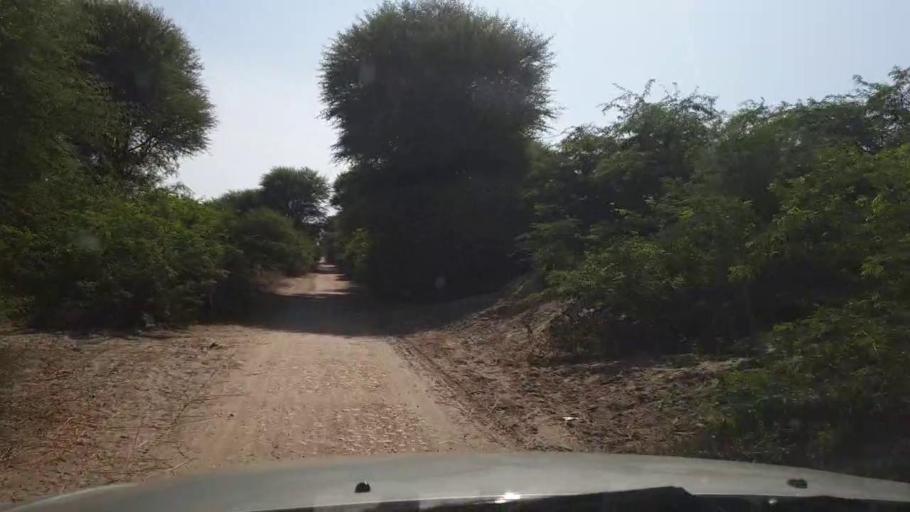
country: PK
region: Sindh
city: Bulri
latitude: 24.9540
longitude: 68.3247
